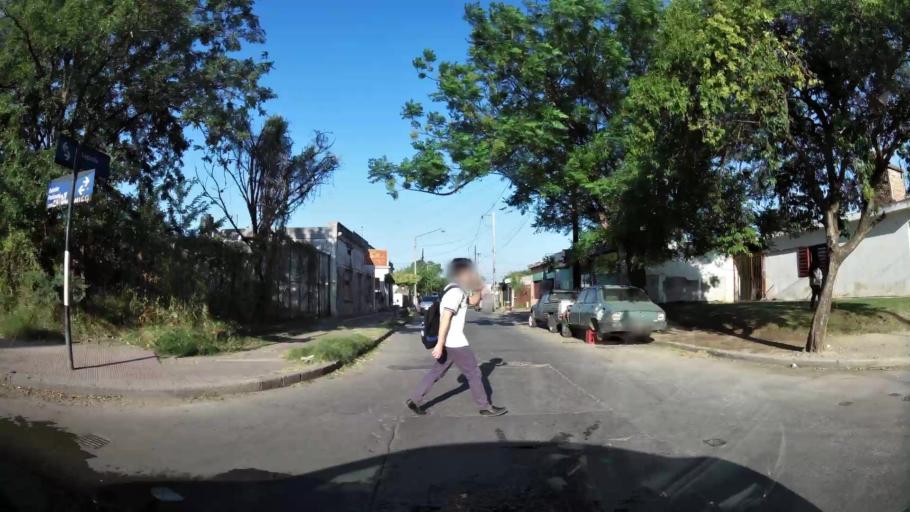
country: AR
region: Cordoba
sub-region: Departamento de Capital
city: Cordoba
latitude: -31.4368
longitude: -64.2480
